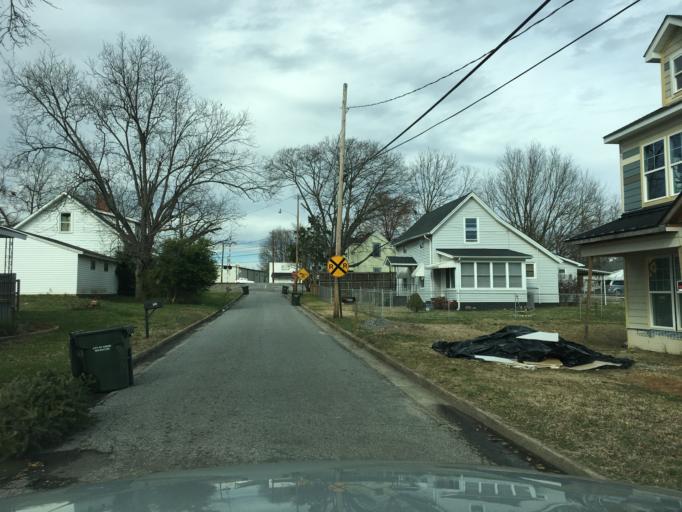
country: US
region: South Carolina
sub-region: Greenville County
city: Greer
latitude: 34.9345
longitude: -82.2199
